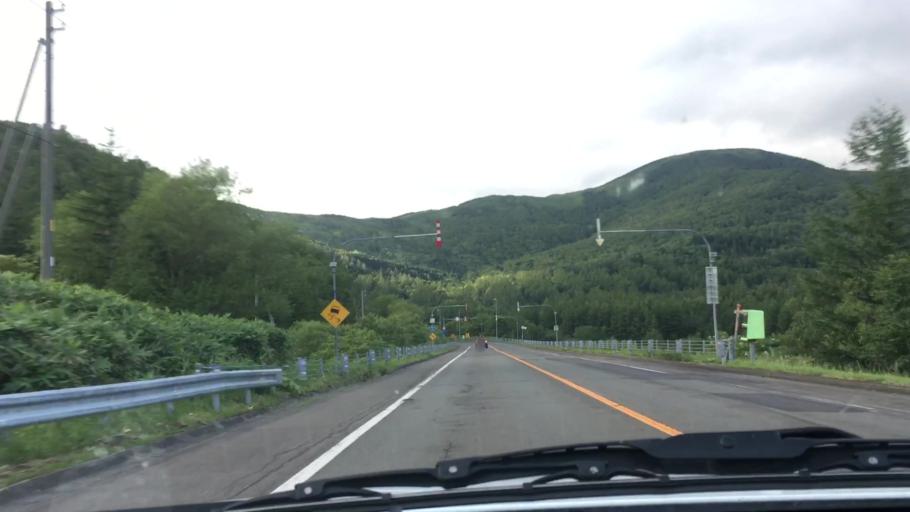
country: JP
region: Hokkaido
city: Shimo-furano
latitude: 43.1360
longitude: 142.7547
